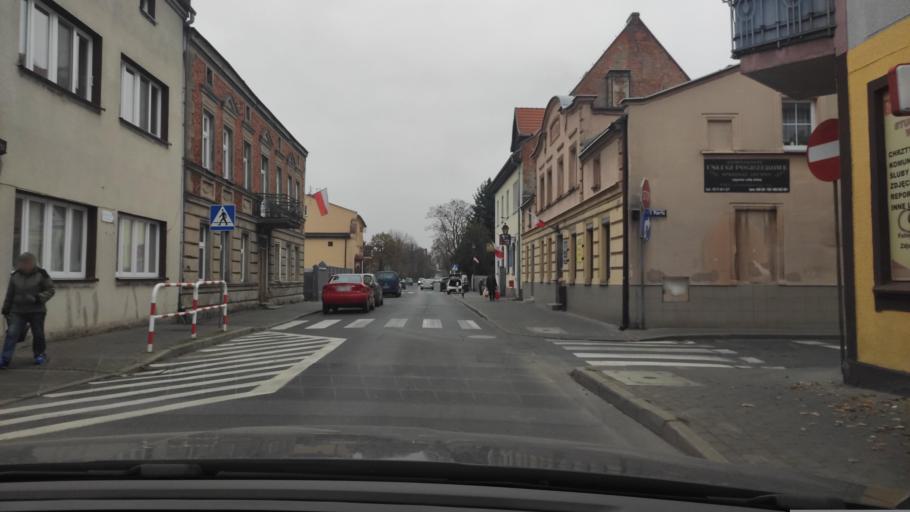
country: PL
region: Greater Poland Voivodeship
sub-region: Powiat poznanski
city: Kostrzyn
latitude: 52.3971
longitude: 17.2262
